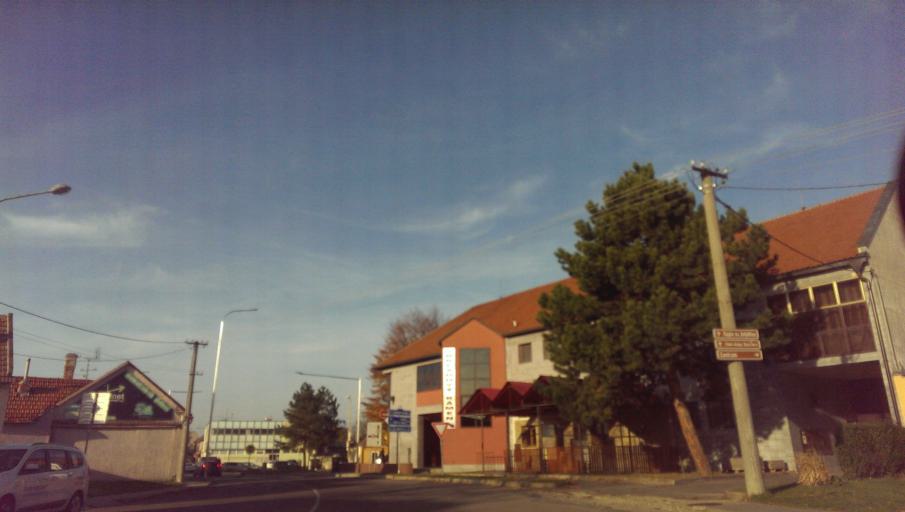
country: CZ
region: Zlin
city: Ostrozska Lhota
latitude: 48.9454
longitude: 17.4628
